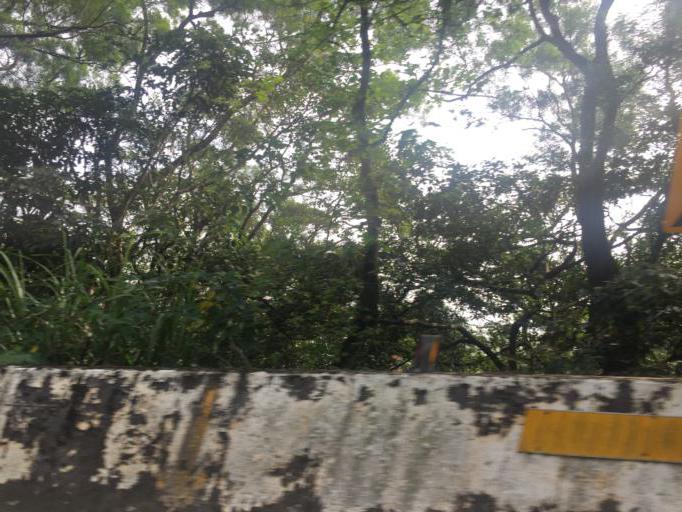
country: TW
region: Taiwan
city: Daxi
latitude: 24.8420
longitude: 121.2114
